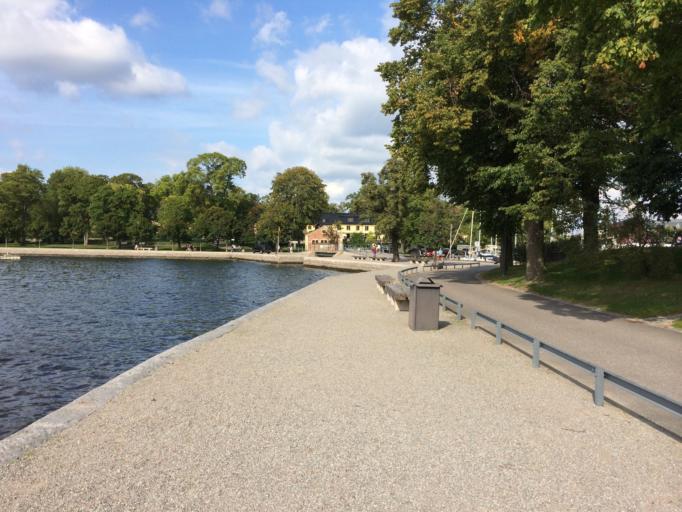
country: SE
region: Stockholm
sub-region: Stockholms Kommun
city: OEstermalm
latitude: 59.3228
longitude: 18.0878
